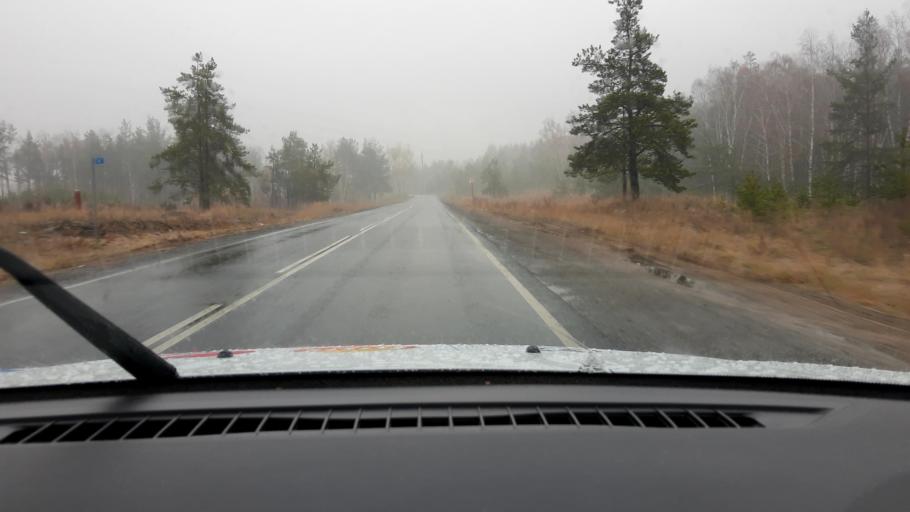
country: RU
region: Nizjnij Novgorod
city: Babino
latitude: 56.2773
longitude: 43.5958
